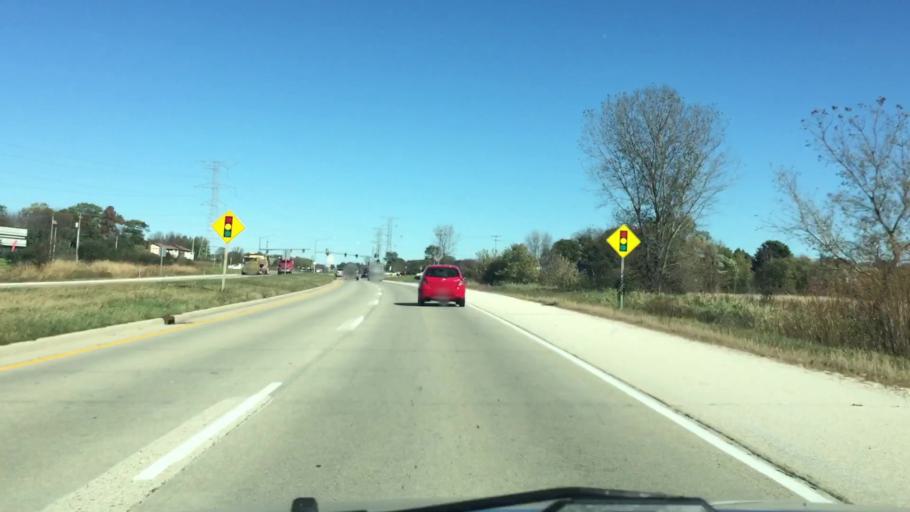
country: US
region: Wisconsin
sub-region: Waukesha County
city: Waukesha
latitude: 42.9841
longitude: -88.2090
